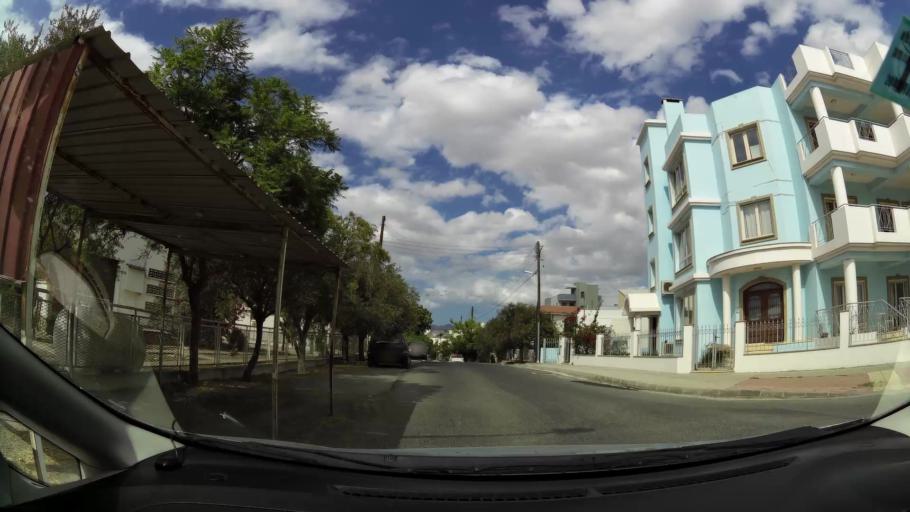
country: CY
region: Lefkosia
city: Nicosia
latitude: 35.1739
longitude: 33.3858
